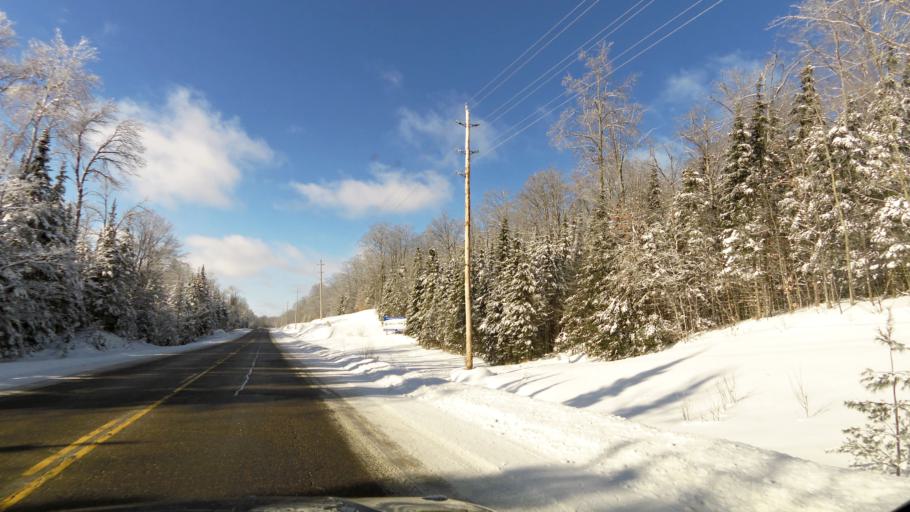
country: CA
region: Ontario
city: Bancroft
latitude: 45.0117
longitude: -78.3246
